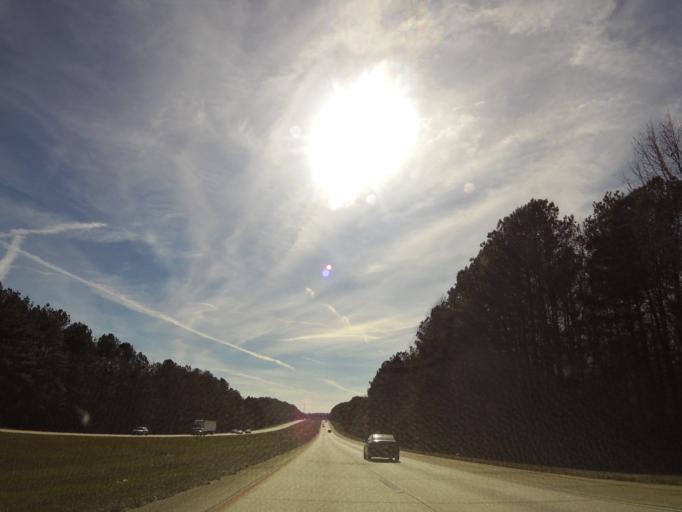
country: US
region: Georgia
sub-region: Coweta County
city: Grantville
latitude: 33.1841
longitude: -84.8563
